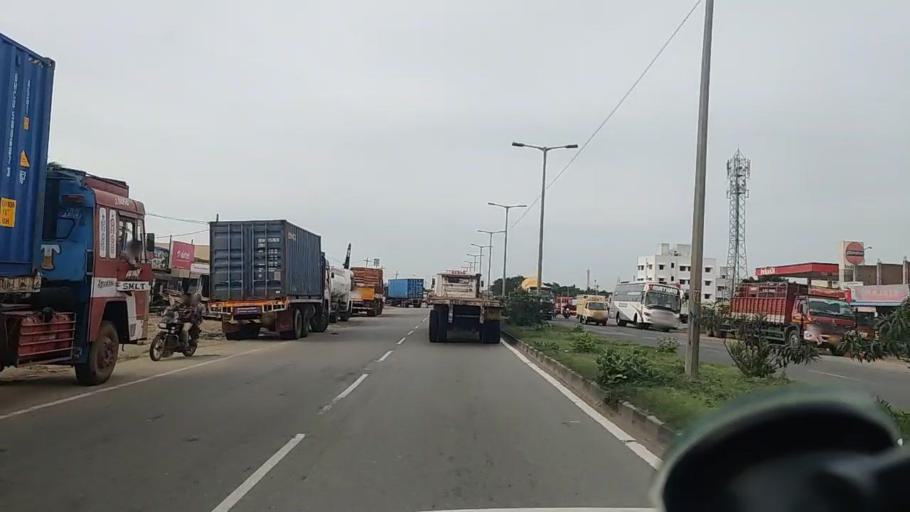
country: IN
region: Tamil Nadu
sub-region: Thiruvallur
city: Chinnasekkadu
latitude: 13.1595
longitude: 80.2262
